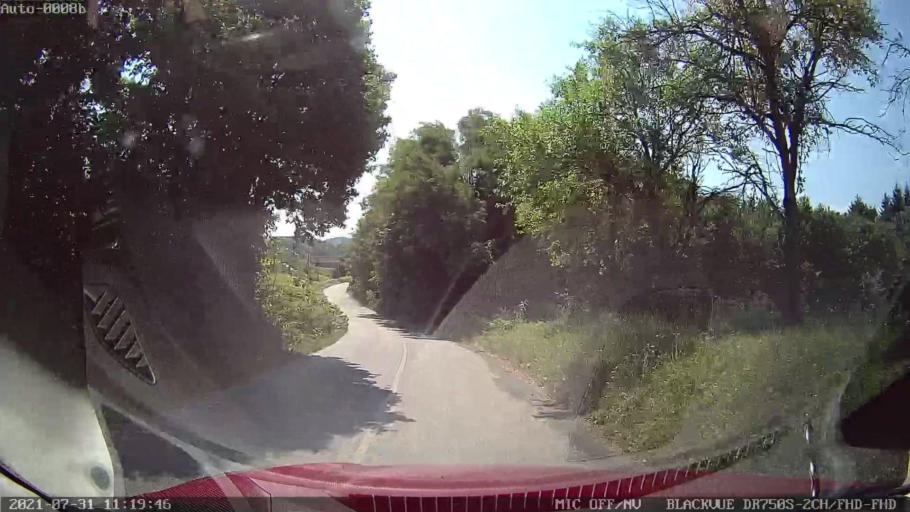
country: HR
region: Varazdinska
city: Jalzabet
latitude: 46.2377
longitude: 16.4749
